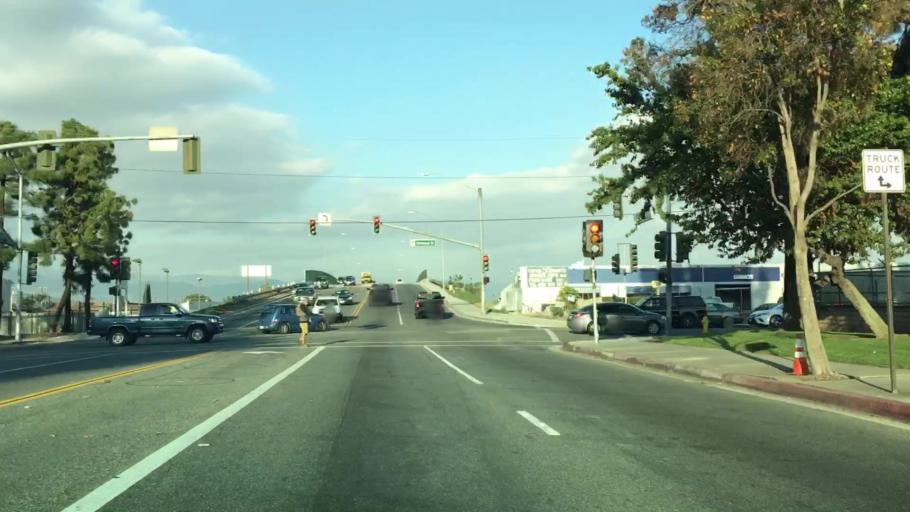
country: US
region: California
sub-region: Los Angeles County
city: West Puente Valley
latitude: 34.0640
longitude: -117.9852
